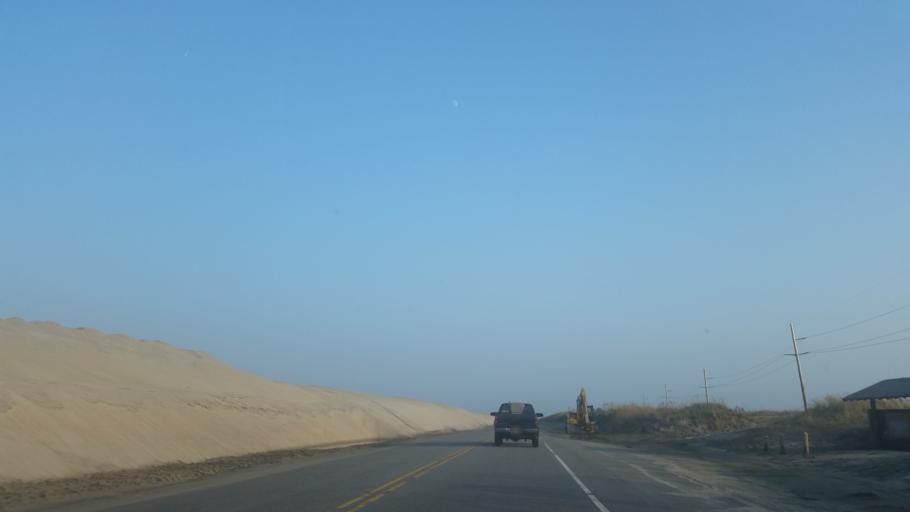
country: US
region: North Carolina
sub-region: Dare County
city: Wanchese
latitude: 35.7615
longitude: -75.5169
